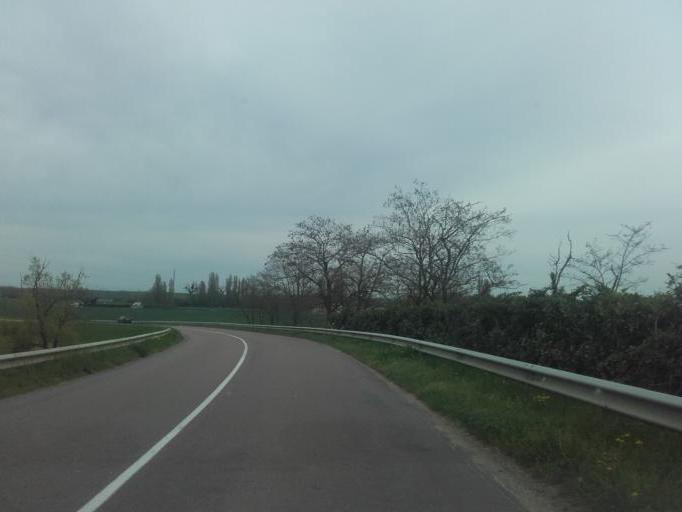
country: FR
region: Bourgogne
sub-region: Departement de la Cote-d'Or
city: Meursault
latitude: 46.9666
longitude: 4.7937
